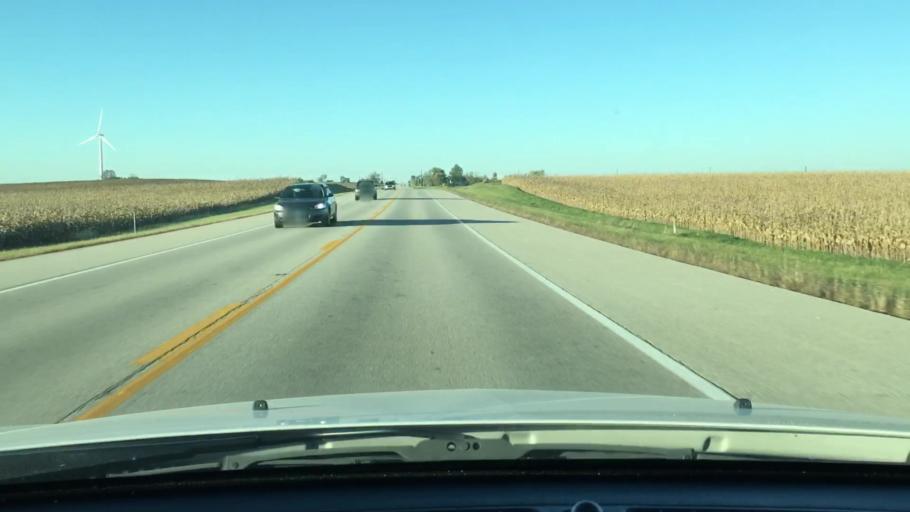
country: US
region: Illinois
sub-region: DeKalb County
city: Waterman
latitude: 41.8111
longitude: -88.7539
